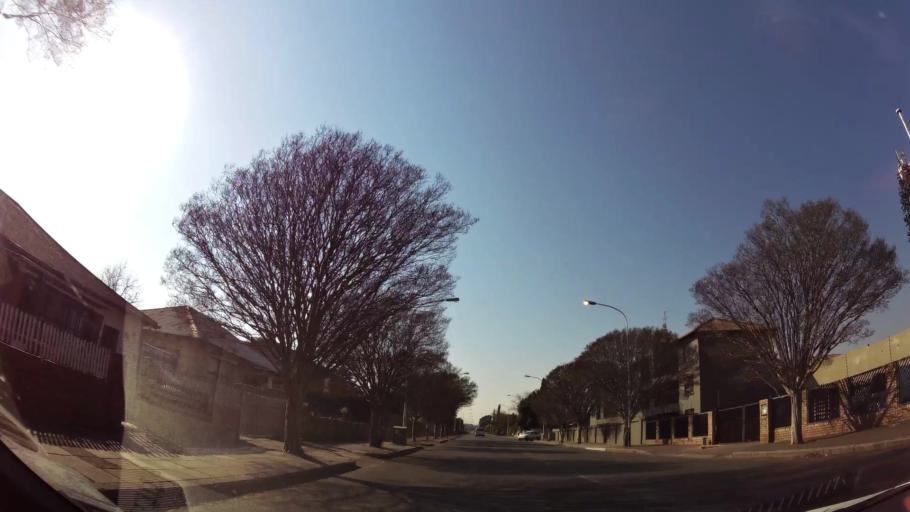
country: ZA
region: Gauteng
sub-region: Ekurhuleni Metropolitan Municipality
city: Boksburg
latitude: -26.2236
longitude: 28.2641
